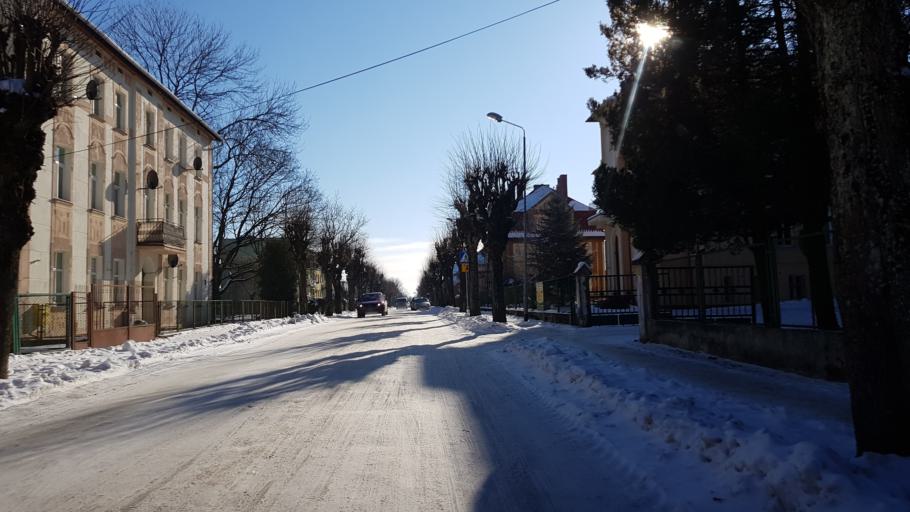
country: PL
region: West Pomeranian Voivodeship
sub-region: Powiat koszalinski
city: Bobolice
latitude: 53.9576
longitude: 16.5896
